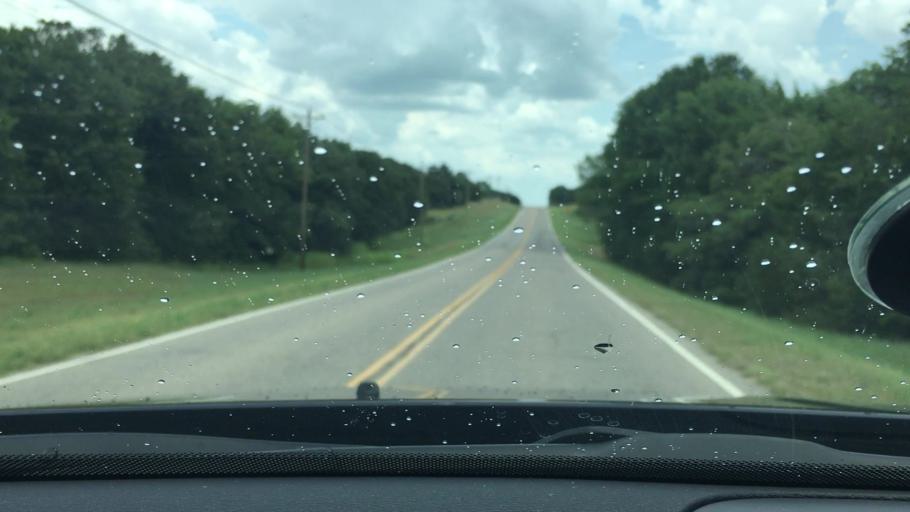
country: US
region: Oklahoma
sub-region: Love County
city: Marietta
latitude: 33.9511
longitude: -97.0327
